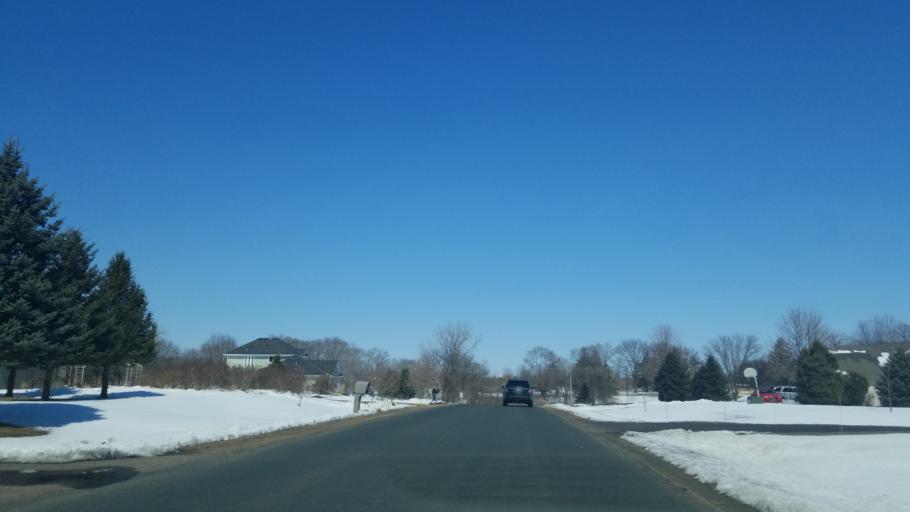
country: US
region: Wisconsin
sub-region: Saint Croix County
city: North Hudson
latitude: 45.0017
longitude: -92.6583
